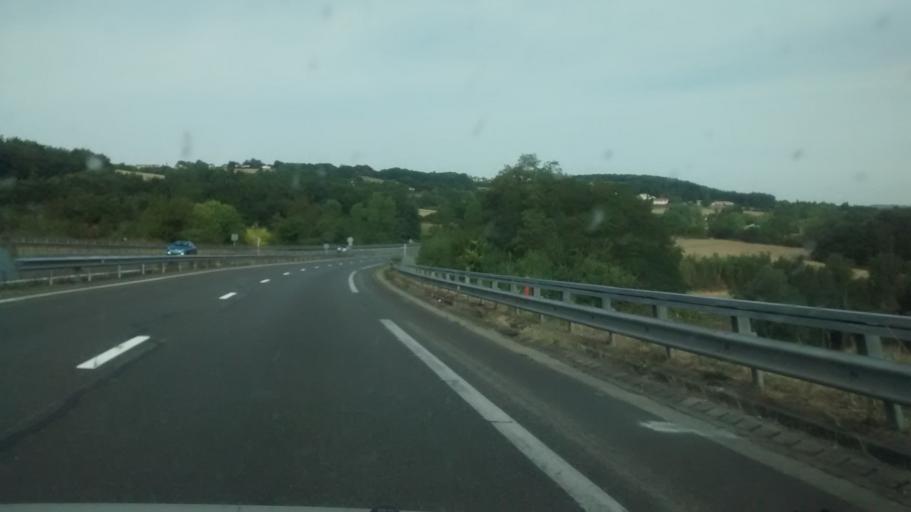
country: FR
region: Aquitaine
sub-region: Departement du Lot-et-Garonne
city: Boe
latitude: 44.1466
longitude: 0.6253
